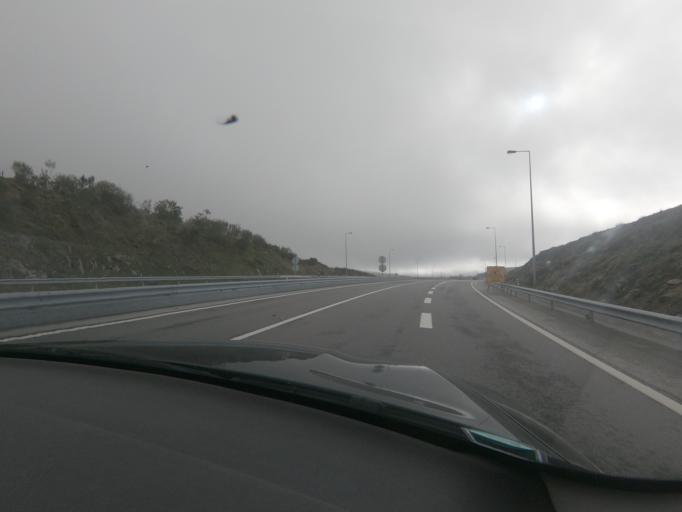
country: PT
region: Viseu
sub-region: Tarouca
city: Tarouca
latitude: 41.0076
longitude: -7.8837
